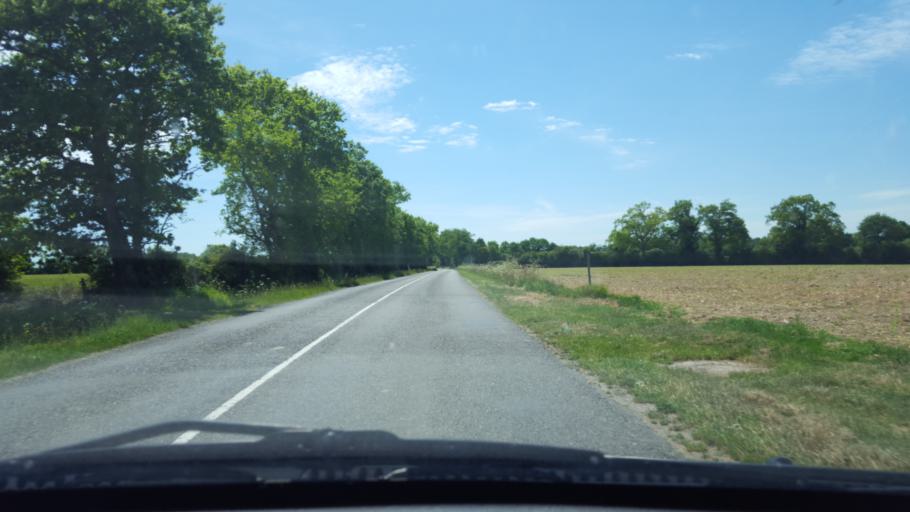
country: FR
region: Pays de la Loire
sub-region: Departement de la Loire-Atlantique
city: Touvois
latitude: 46.9327
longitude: -1.6795
